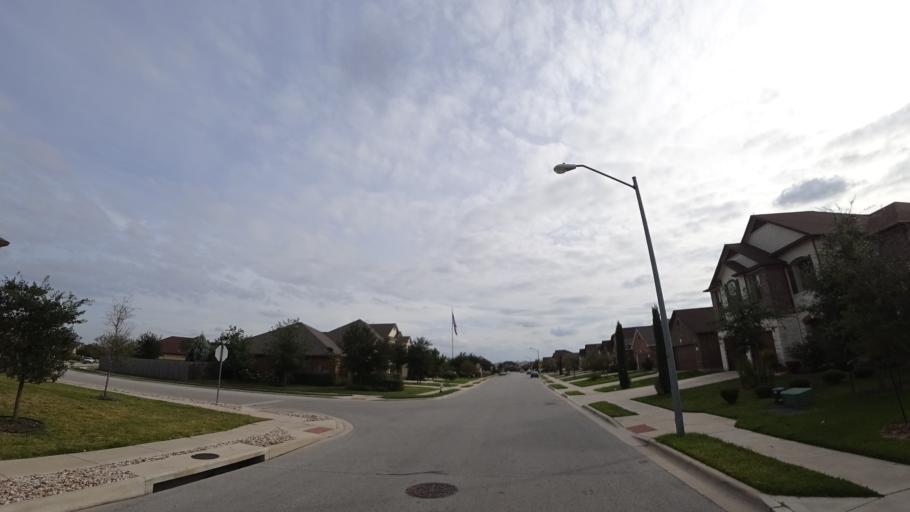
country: US
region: Texas
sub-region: Travis County
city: Wells Branch
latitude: 30.4299
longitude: -97.6626
